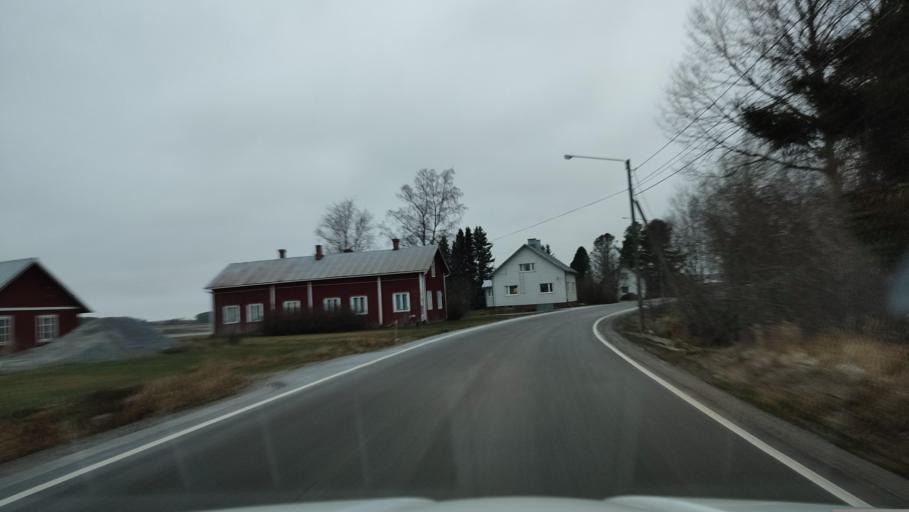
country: FI
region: Southern Ostrobothnia
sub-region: Suupohja
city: Karijoki
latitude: 62.2404
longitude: 21.5650
